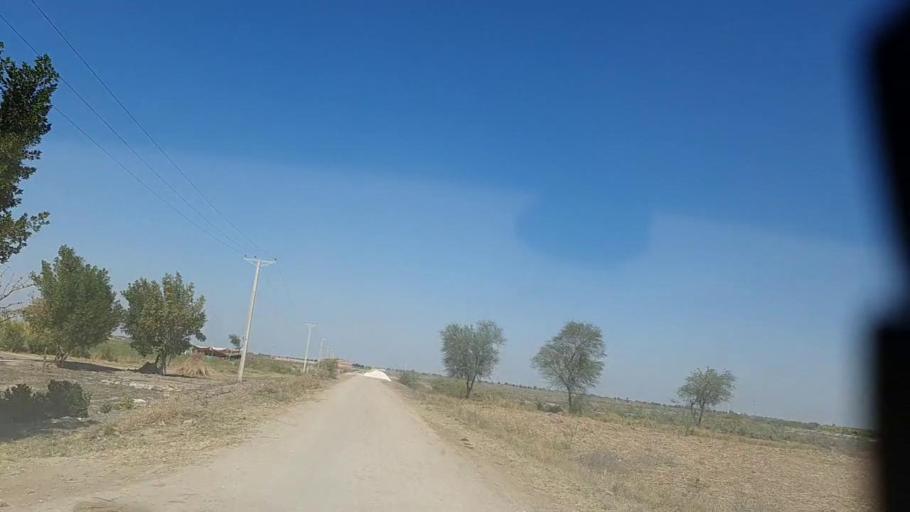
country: PK
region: Sindh
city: Digri
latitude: 25.1531
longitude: 69.0487
